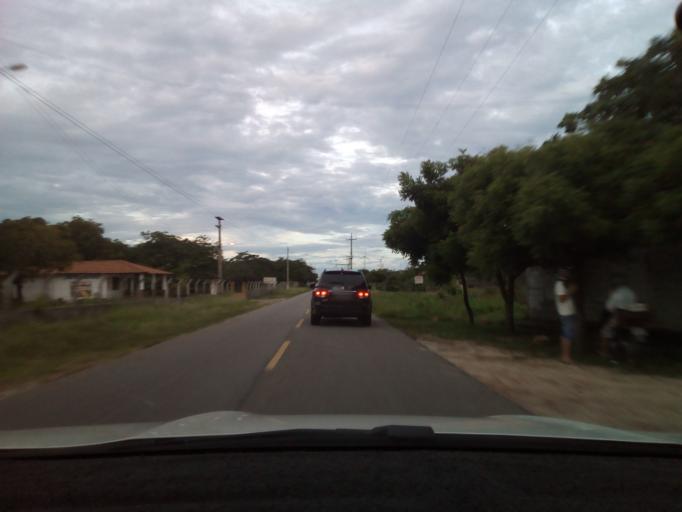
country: BR
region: Ceara
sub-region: Beberibe
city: Beberibe
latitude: -4.1852
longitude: -38.1044
